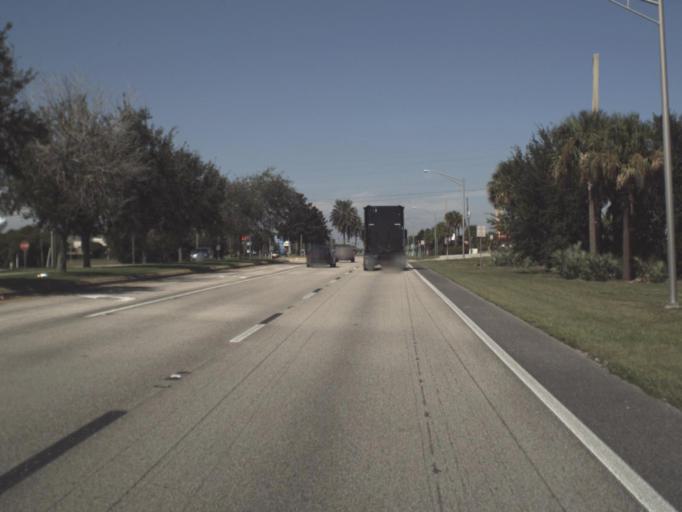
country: US
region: Florida
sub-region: Highlands County
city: Lake Placid
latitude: 27.2916
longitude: -81.3582
